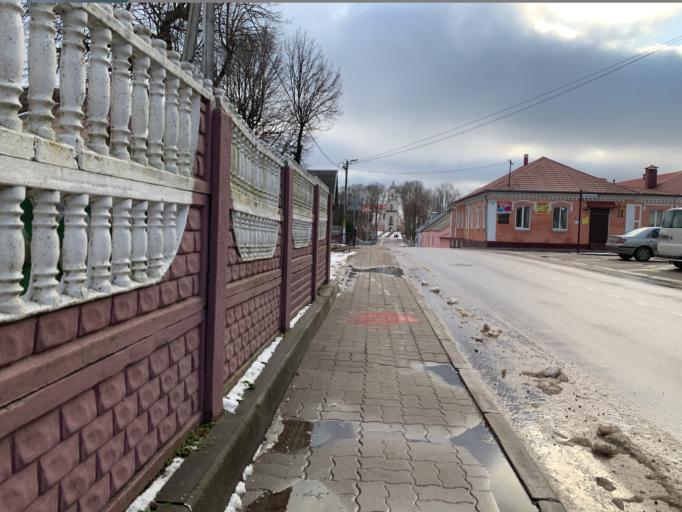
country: BY
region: Minsk
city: Nyasvizh
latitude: 53.2183
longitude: 26.6834
